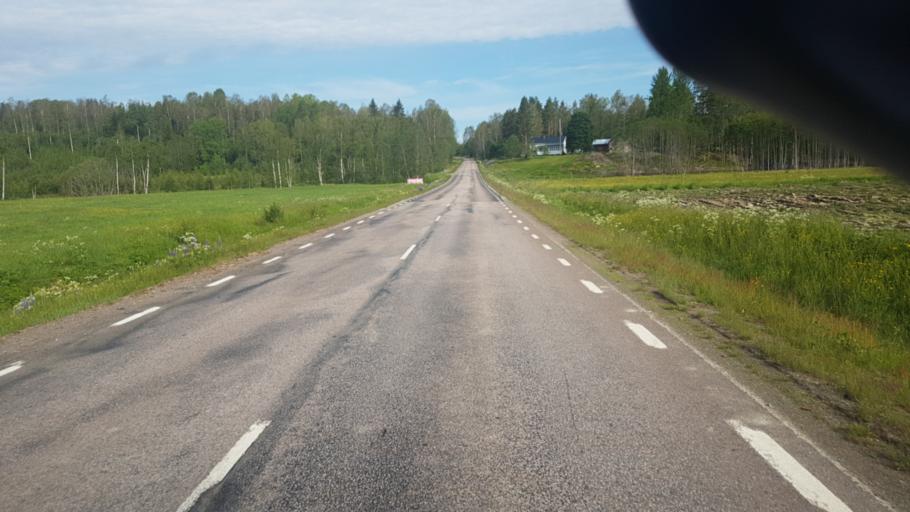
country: SE
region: Vaermland
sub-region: Arvika Kommun
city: Arvika
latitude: 59.8100
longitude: 12.5918
